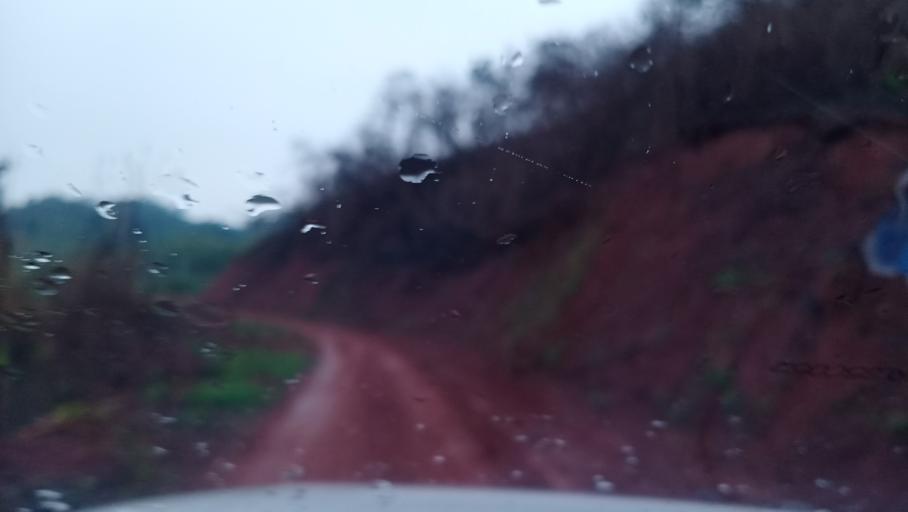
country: CN
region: Yunnan
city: Menglie
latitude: 22.2245
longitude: 101.6414
